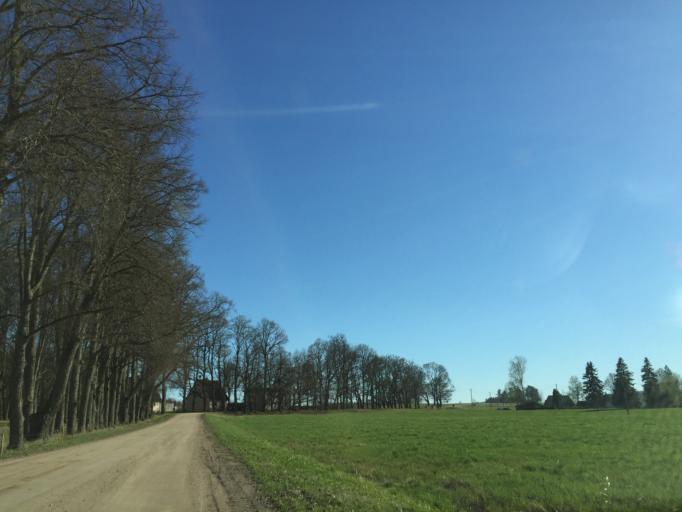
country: EE
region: Valgamaa
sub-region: Valga linn
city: Valga
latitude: 57.7639
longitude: 26.2095
